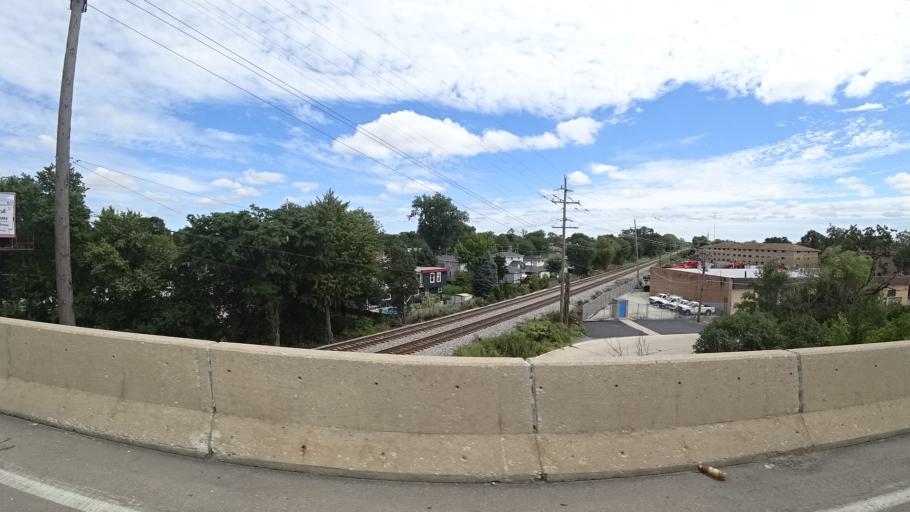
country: US
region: Illinois
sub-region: Cook County
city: Chicago Ridge
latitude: 41.7167
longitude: -87.7983
